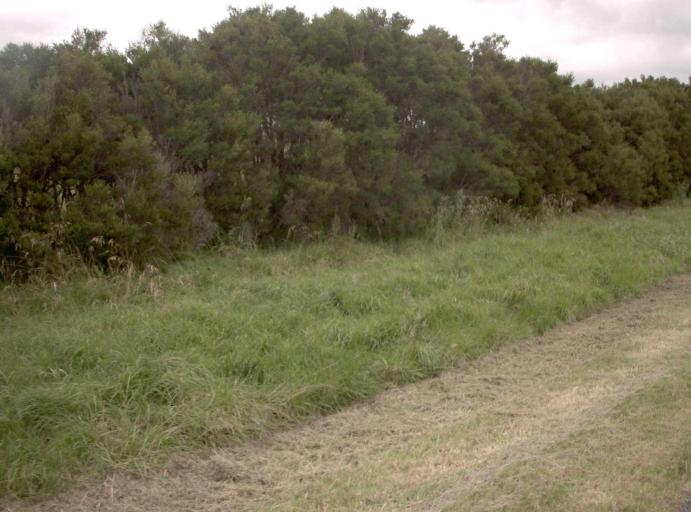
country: AU
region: Victoria
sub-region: Bass Coast
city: North Wonthaggi
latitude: -38.5891
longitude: 145.6152
